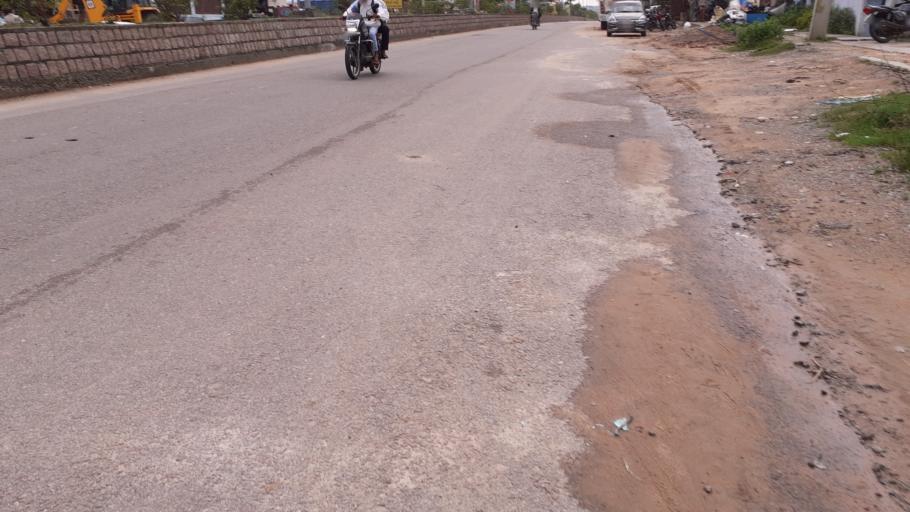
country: IN
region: Telangana
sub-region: Medak
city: Medak
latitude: 18.0317
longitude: 78.2622
